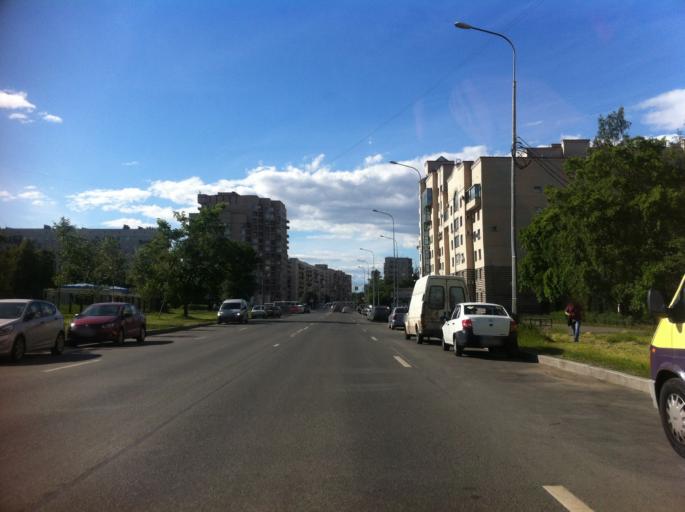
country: RU
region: St.-Petersburg
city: Dachnoye
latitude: 59.8387
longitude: 30.2408
